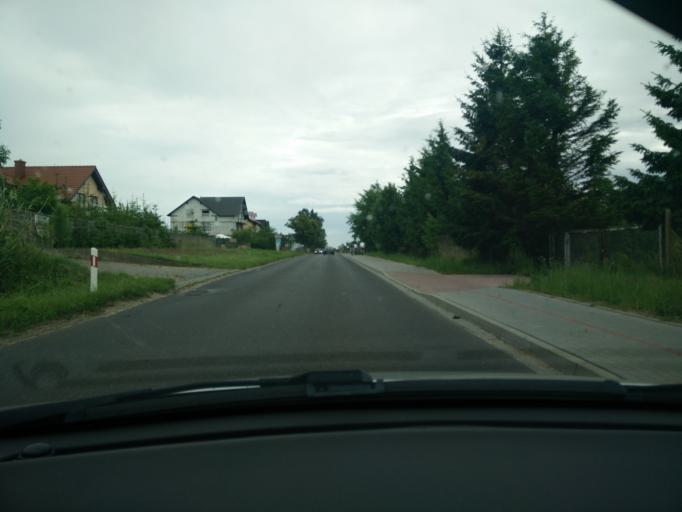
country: PL
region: Pomeranian Voivodeship
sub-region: Powiat pucki
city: Mosty
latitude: 54.6214
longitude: 18.4963
